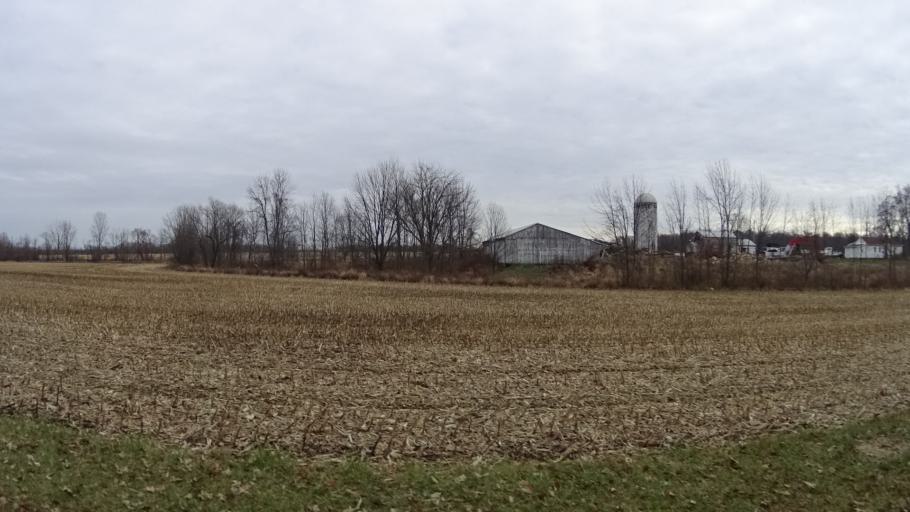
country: US
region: Ohio
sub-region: Lorain County
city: Wellington
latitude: 41.1318
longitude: -82.1943
